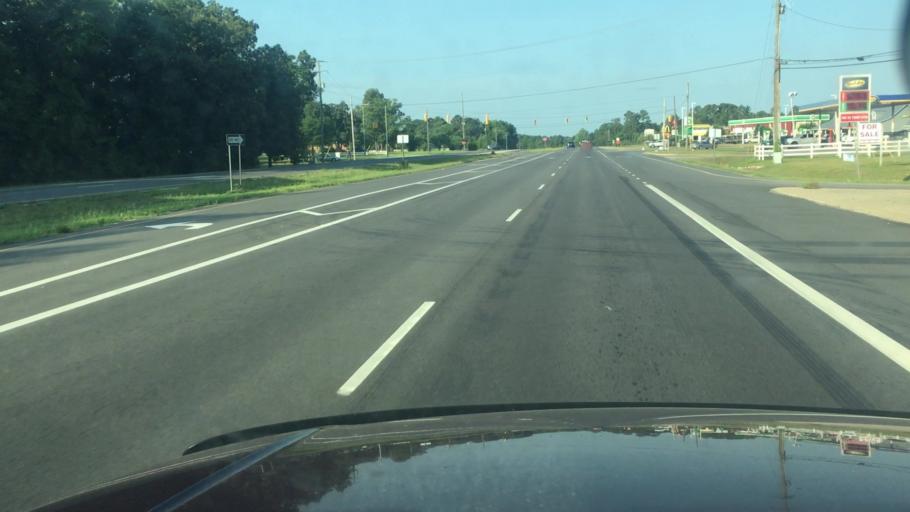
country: US
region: North Carolina
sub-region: Cumberland County
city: Hope Mills
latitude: 34.9313
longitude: -78.8525
